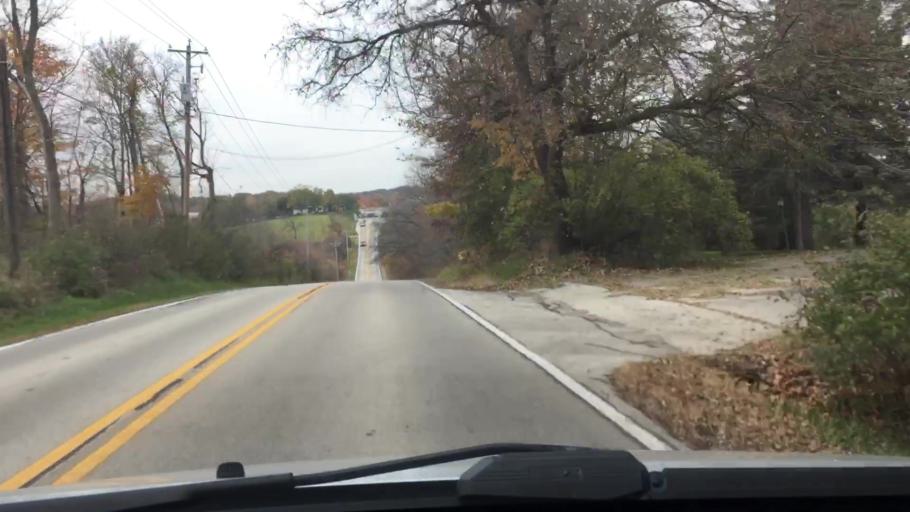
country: US
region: Wisconsin
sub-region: Waukesha County
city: New Berlin
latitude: 42.9445
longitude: -88.0996
